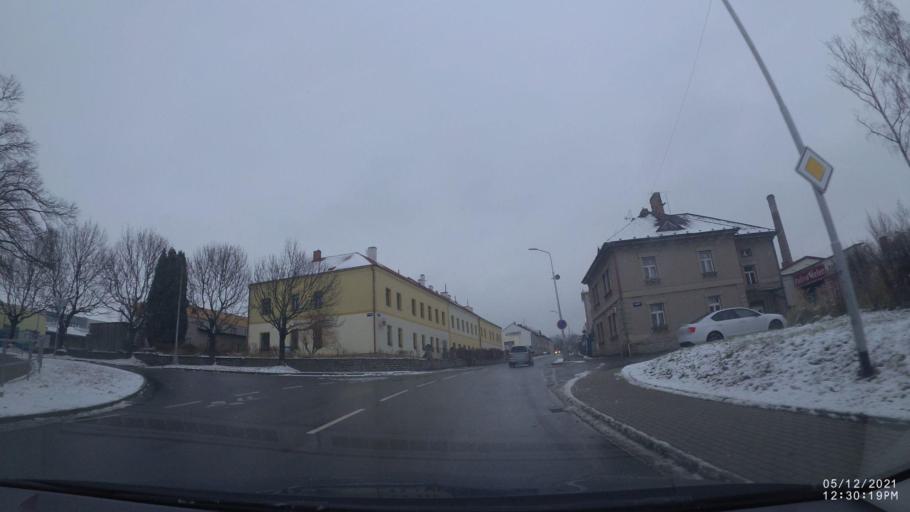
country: CZ
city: Nove Mesto nad Metuji
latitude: 50.3524
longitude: 16.1383
